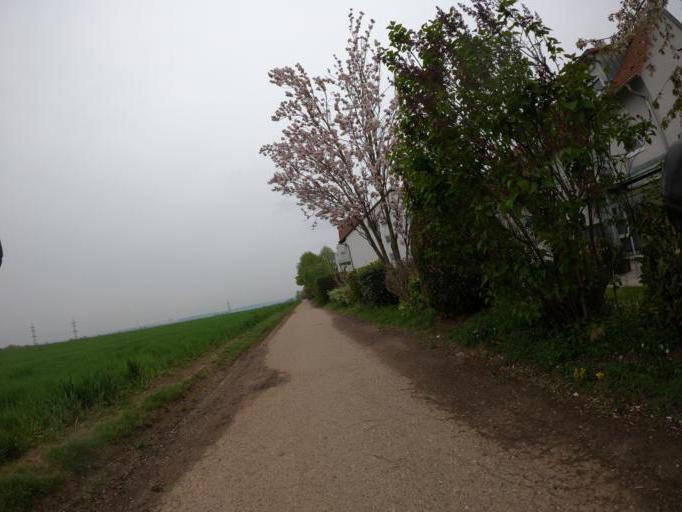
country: DE
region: Baden-Wuerttemberg
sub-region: Regierungsbezirk Stuttgart
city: Vaihingen an der Enz
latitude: 48.9486
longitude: 8.9703
